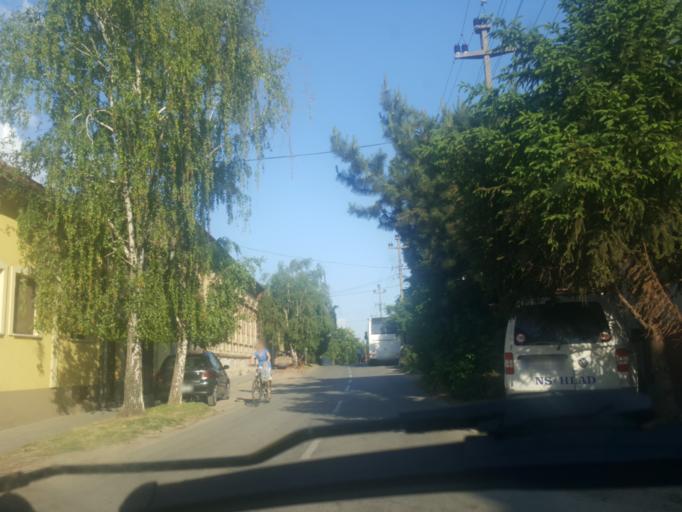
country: RS
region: Autonomna Pokrajina Vojvodina
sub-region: Juznobacki Okrug
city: Sremski Karlovci
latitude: 45.1995
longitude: 19.9397
